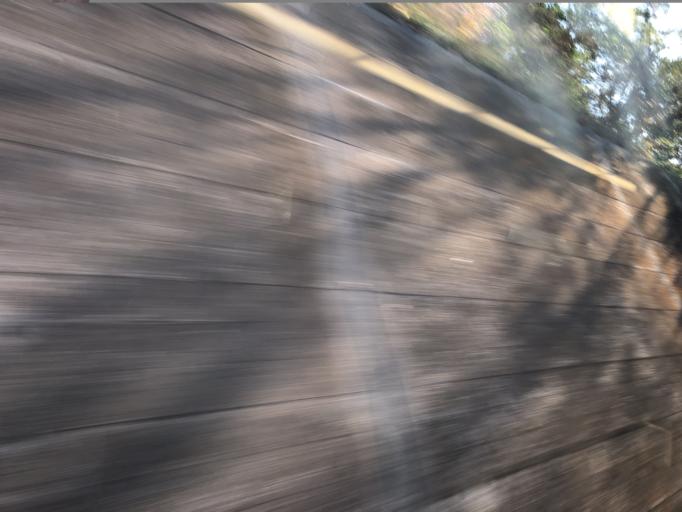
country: JP
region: Kochi
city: Nakamura
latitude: 33.0102
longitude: 132.9890
